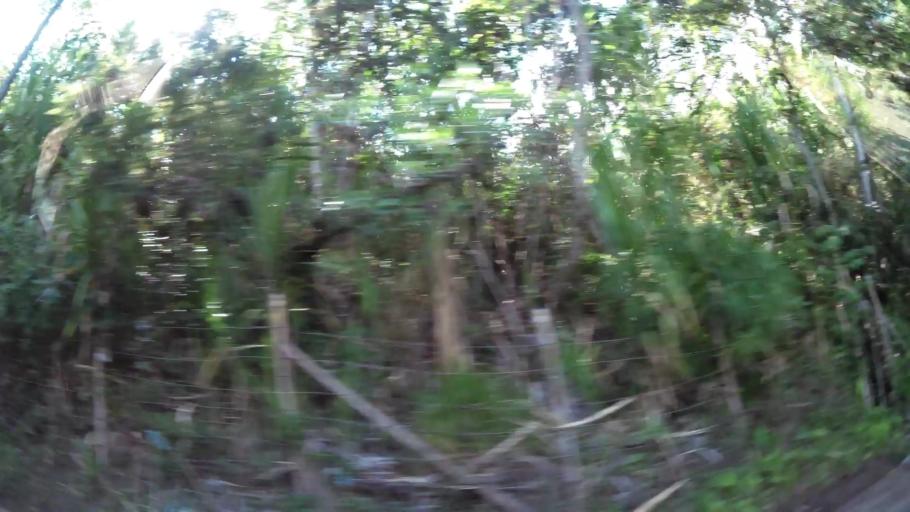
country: CO
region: Valle del Cauca
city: Cali
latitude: 3.4337
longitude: -76.5612
